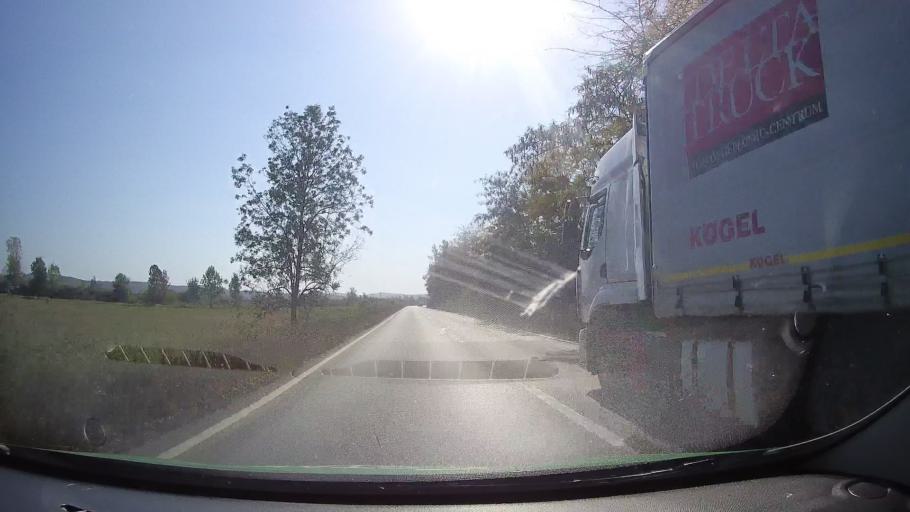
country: RO
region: Arad
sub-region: Comuna Ususau
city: Ususau
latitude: 46.1032
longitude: 21.8149
